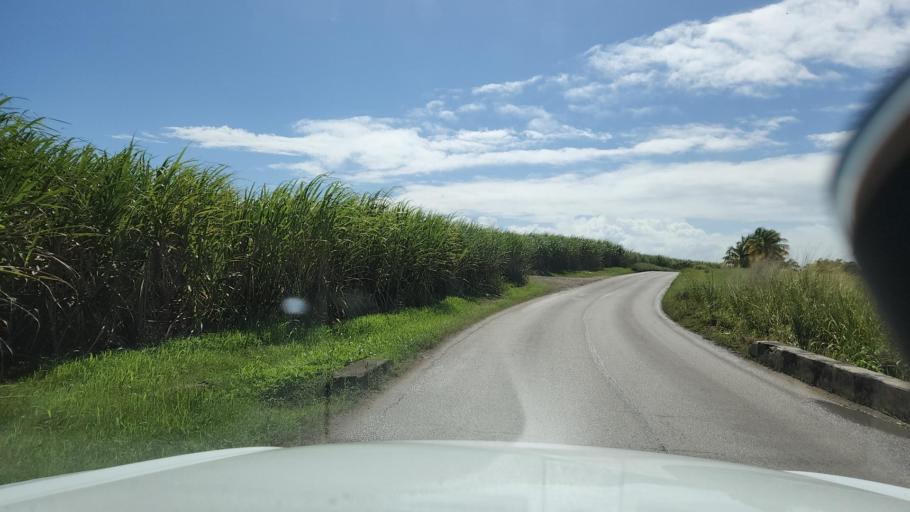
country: BB
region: Christ Church
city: Oistins
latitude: 13.0886
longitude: -59.5289
